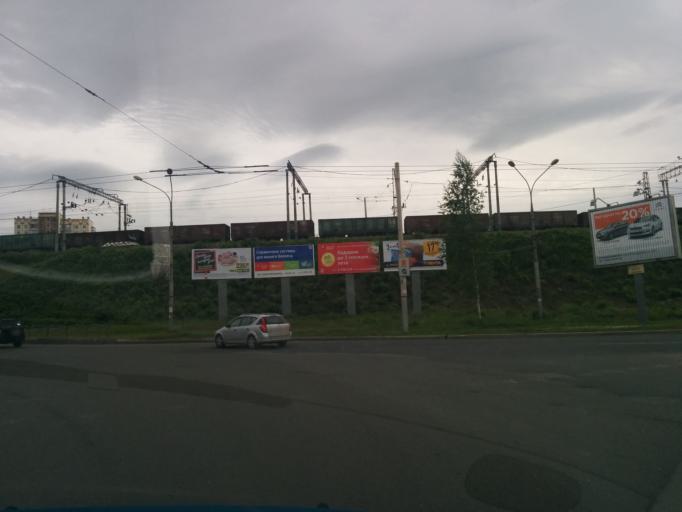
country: RU
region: Perm
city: Perm
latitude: 58.0042
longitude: 56.1939
